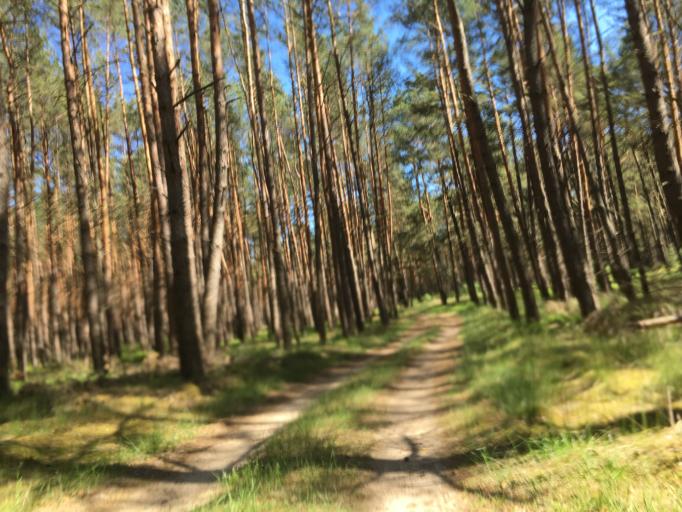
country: DE
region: Brandenburg
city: Friedrichswalde
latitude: 52.9661
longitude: 13.6493
